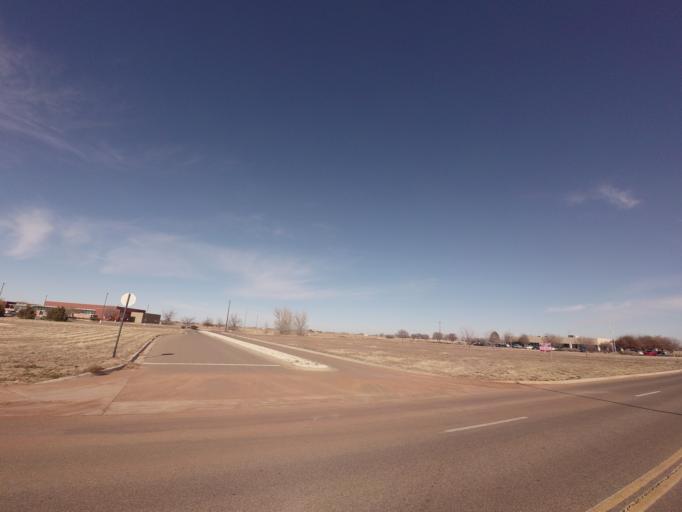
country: US
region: New Mexico
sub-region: Curry County
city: Clovis
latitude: 34.4049
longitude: -103.1666
